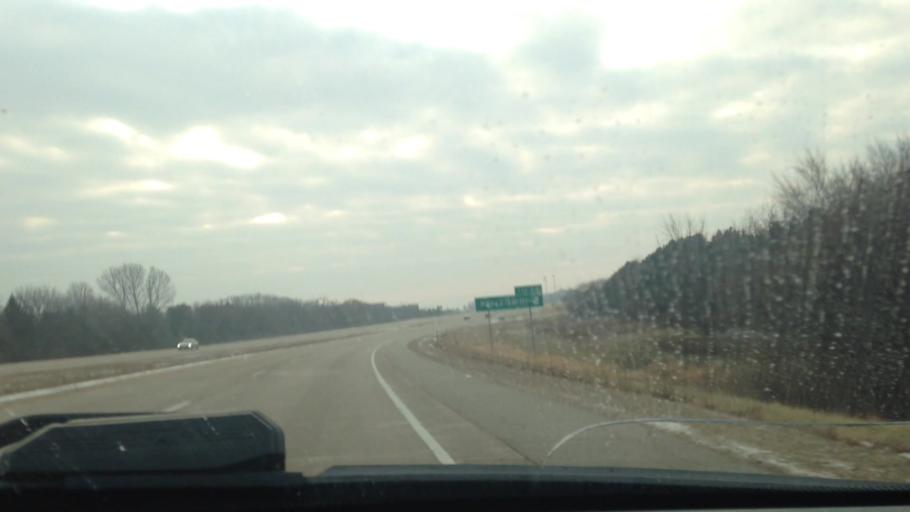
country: US
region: Wisconsin
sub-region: Washington County
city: West Bend
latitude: 43.4043
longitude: -88.1955
